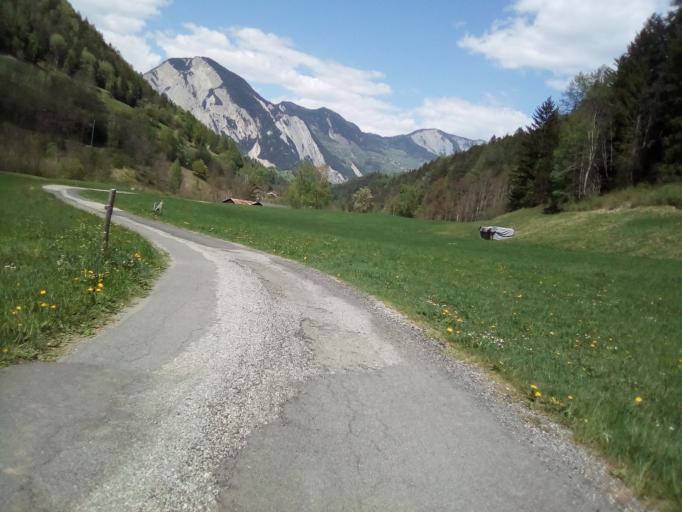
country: CH
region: Valais
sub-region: Entremont District
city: Orsieres
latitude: 46.0483
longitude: 7.1493
